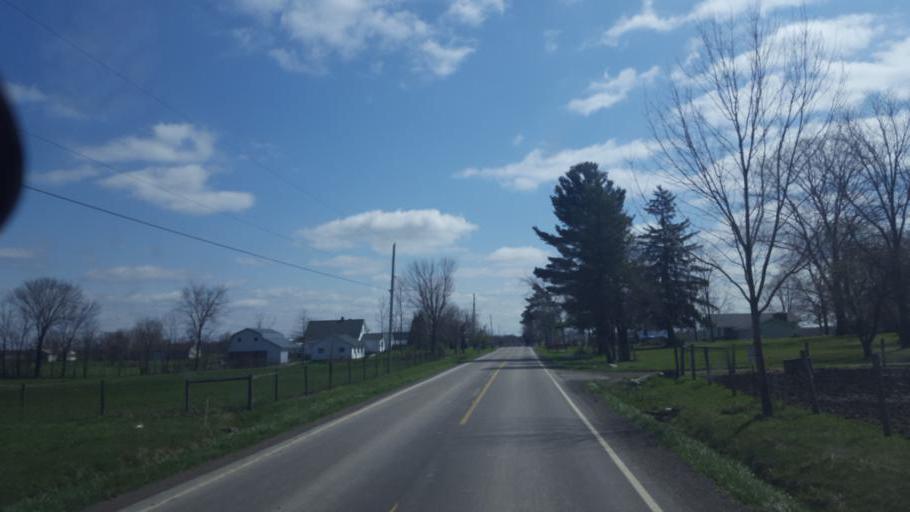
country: US
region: Ohio
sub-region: Geauga County
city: Middlefield
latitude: 41.3869
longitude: -81.1058
